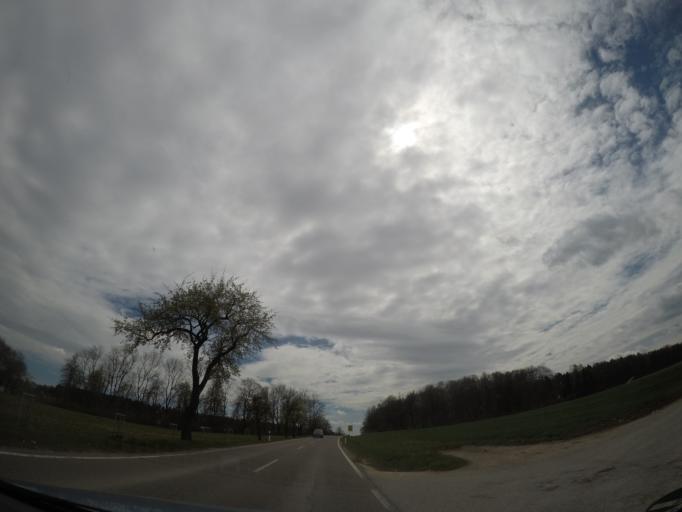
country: DE
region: Baden-Wuerttemberg
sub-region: Tuebingen Region
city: Laichingen
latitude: 48.4828
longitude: 9.6855
